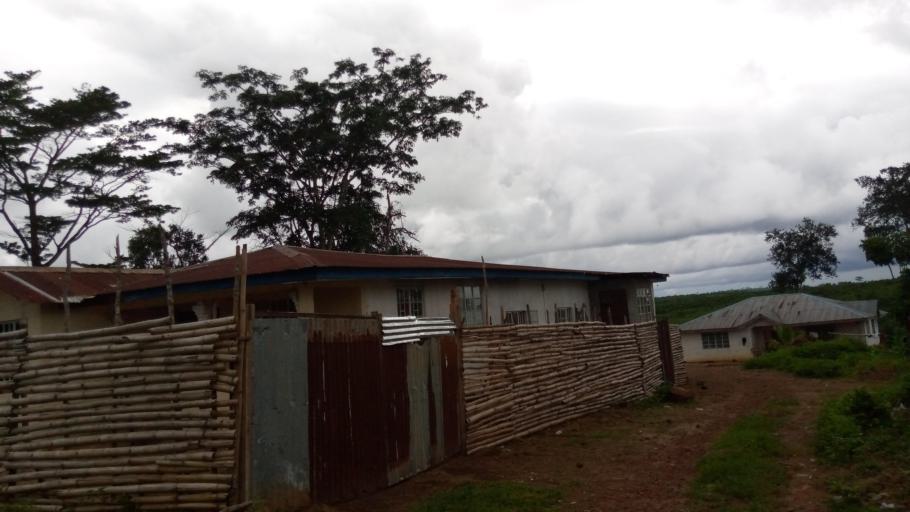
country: SL
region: Southern Province
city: Moyamba
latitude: 8.1642
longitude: -12.4442
